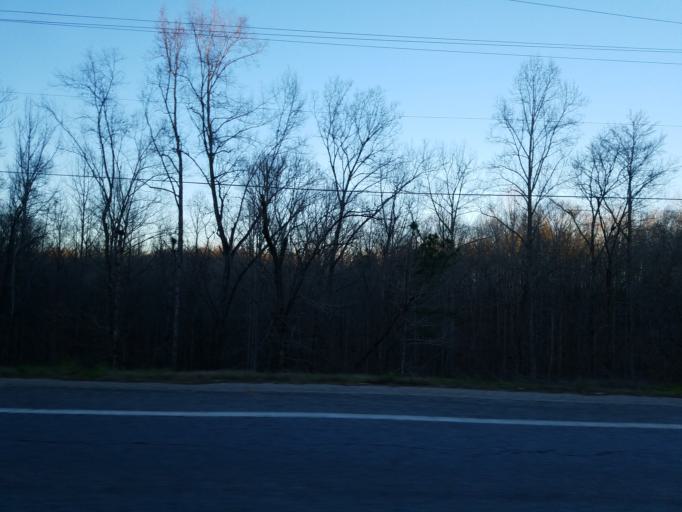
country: US
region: Georgia
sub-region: Dawson County
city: Dawsonville
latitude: 34.3294
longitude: -84.0105
